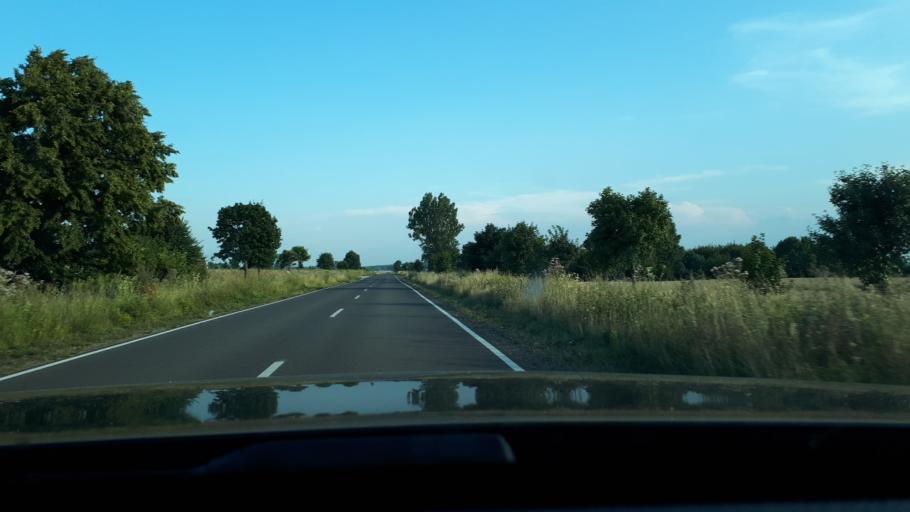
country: PL
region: Warmian-Masurian Voivodeship
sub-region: Powiat nidzicki
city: Nidzica
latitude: 53.4268
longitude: 20.3341
